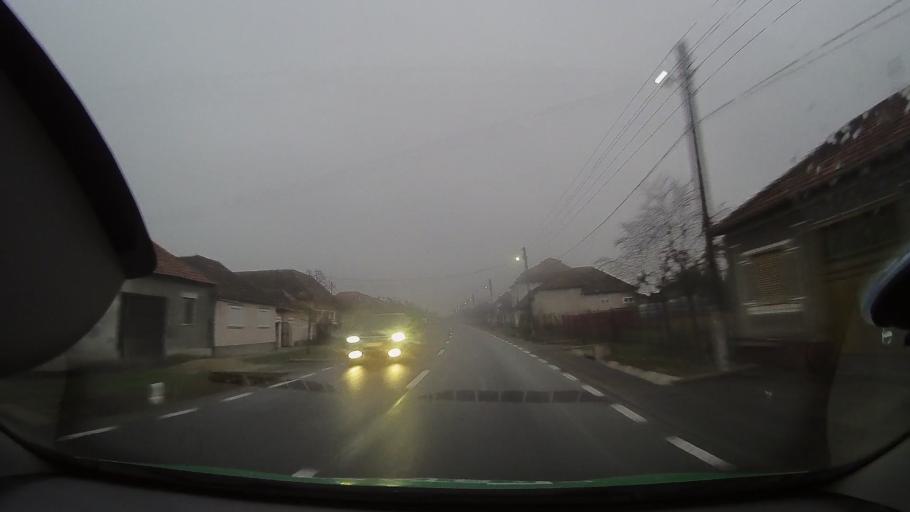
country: RO
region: Bihor
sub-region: Comuna Olcea
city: Calacea
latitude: 46.6359
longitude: 21.9562
